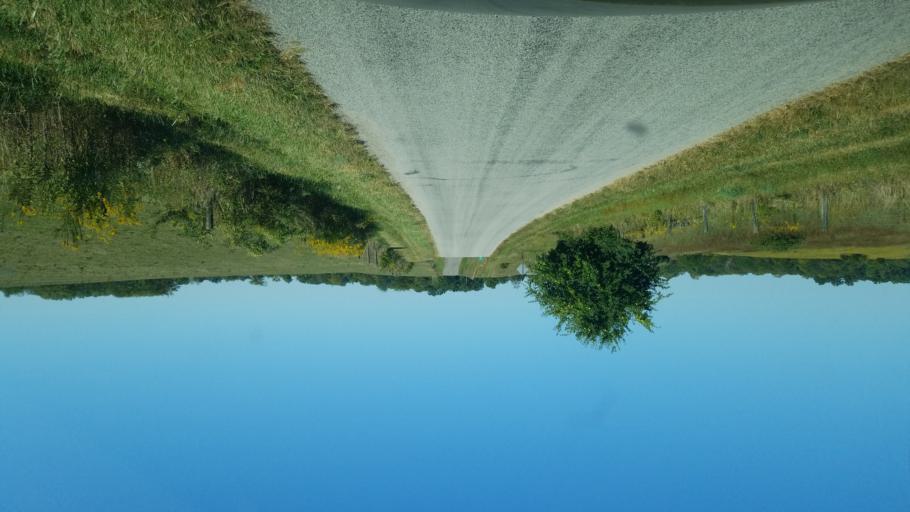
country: US
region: Ohio
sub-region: Champaign County
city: Mechanicsburg
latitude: 40.1148
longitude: -83.5976
